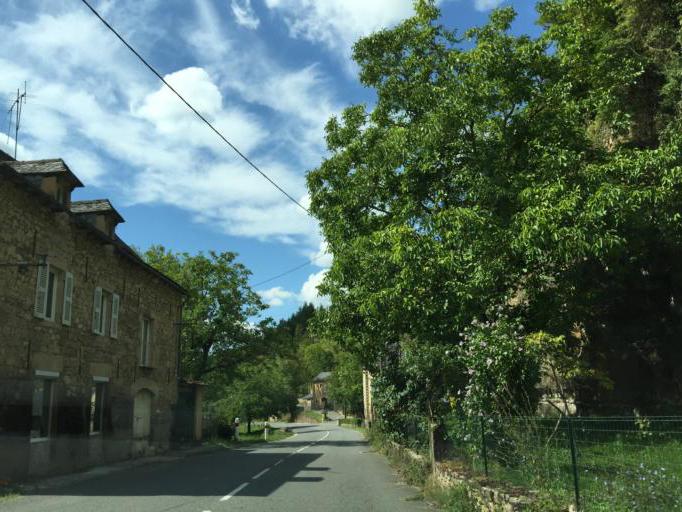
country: FR
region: Midi-Pyrenees
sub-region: Departement de l'Aveyron
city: Salles-la-Source
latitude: 44.4445
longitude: 2.4947
